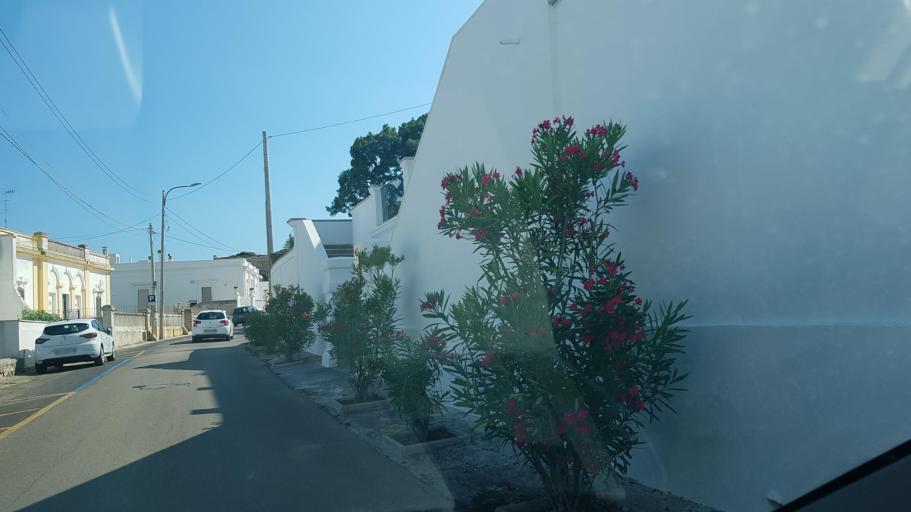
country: IT
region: Apulia
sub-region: Provincia di Lecce
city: Leuca
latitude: 39.7951
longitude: 18.3517
